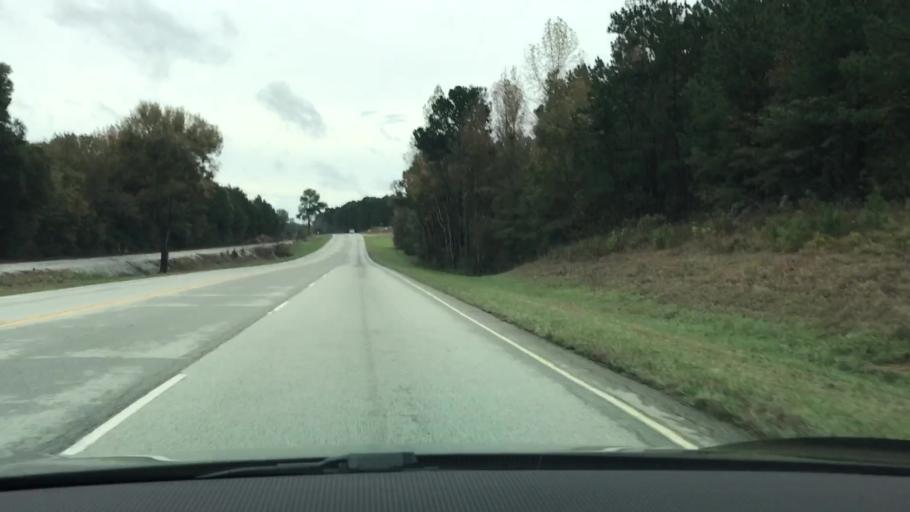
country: US
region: Georgia
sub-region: Taliaferro County
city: Crawfordville
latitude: 33.4899
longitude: -82.7977
